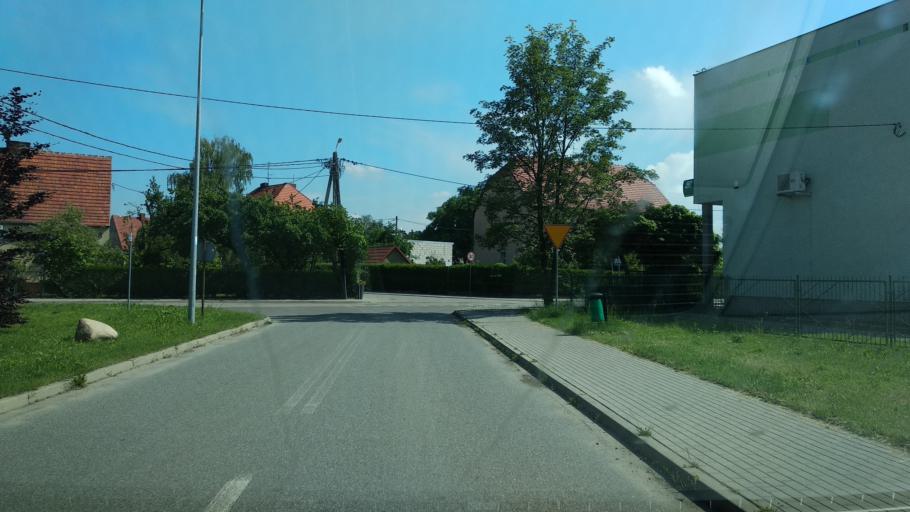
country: PL
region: Lower Silesian Voivodeship
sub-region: Powiat wroclawski
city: Zorawina
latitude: 50.9822
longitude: 17.0436
